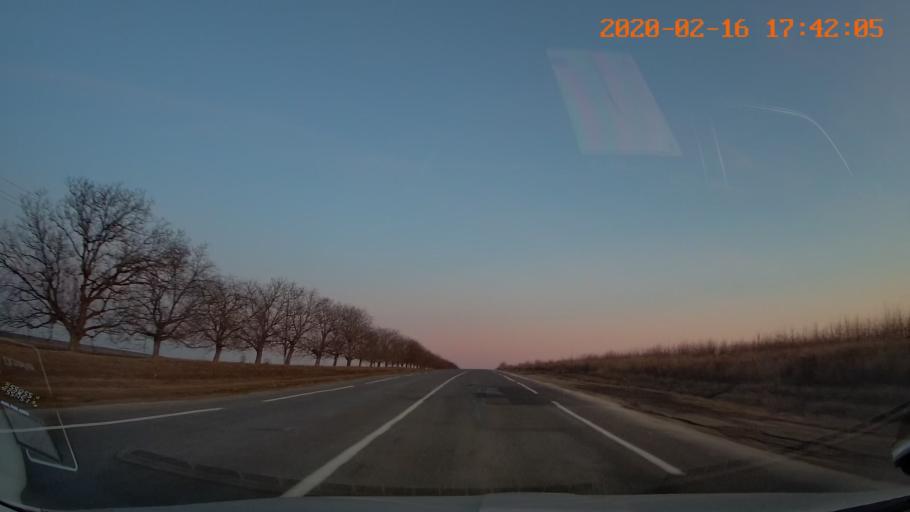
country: MD
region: Riscani
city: Riscani
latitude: 48.0247
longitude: 27.5422
